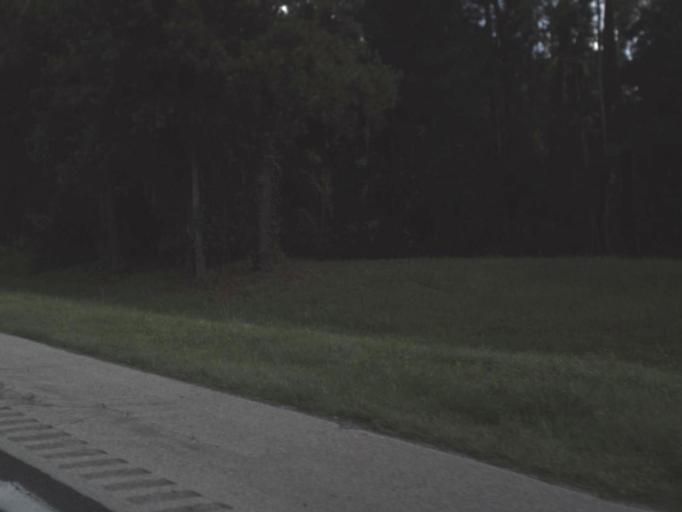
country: US
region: Florida
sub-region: Alachua County
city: Gainesville
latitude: 29.5374
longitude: -82.3253
